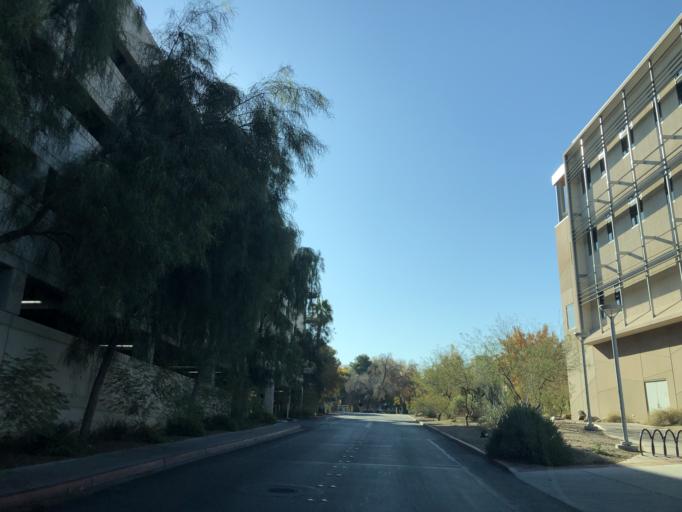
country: US
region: Nevada
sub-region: Clark County
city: Paradise
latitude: 36.1114
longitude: -115.1408
